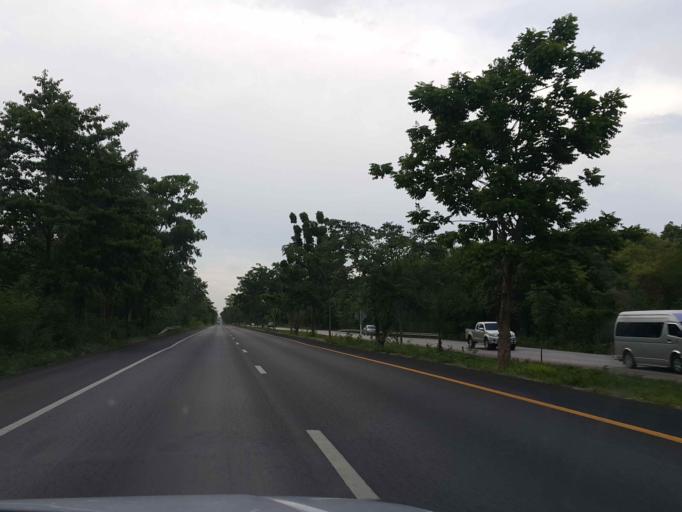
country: TH
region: Lampang
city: Ko Kha
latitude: 18.0765
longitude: 99.3929
